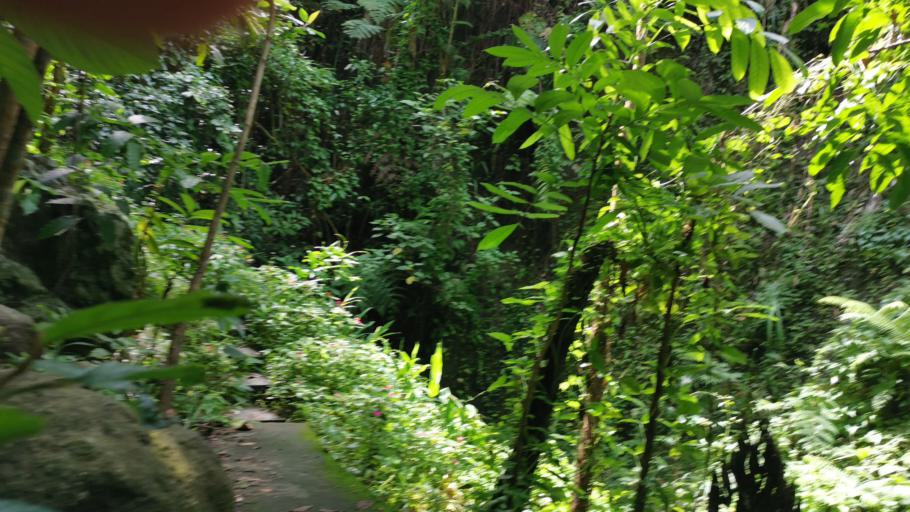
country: PH
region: Cordillera
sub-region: Province of Benguet
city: Bayabas
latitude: 16.4233
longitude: 120.5293
